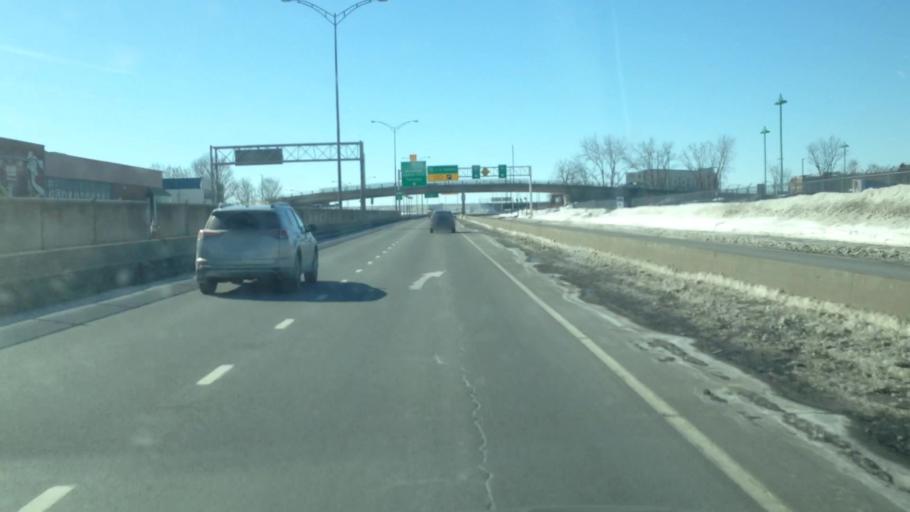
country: CA
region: Quebec
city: Dorval
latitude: 45.4548
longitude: -73.7349
